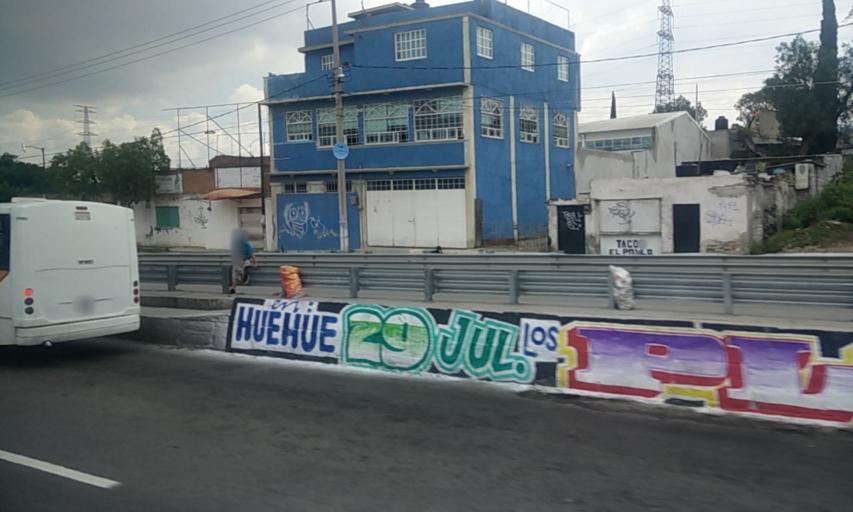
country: MX
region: Morelos
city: Coyotepec
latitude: 19.7763
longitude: -99.2180
